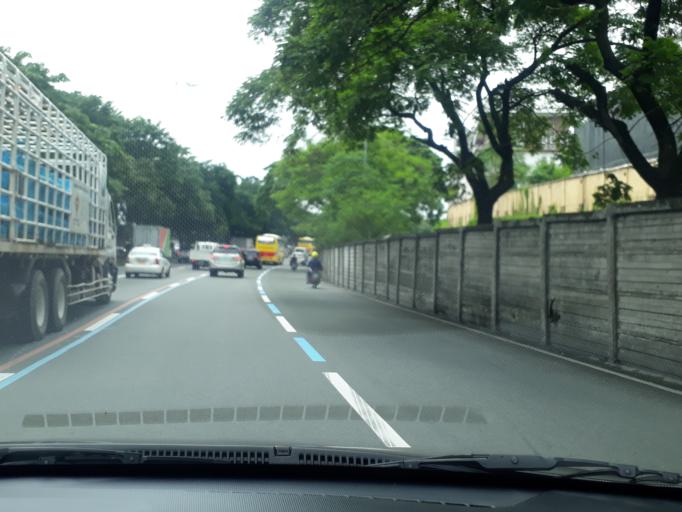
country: PH
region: Calabarzon
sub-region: Province of Rizal
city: Pateros
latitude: 14.5404
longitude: 121.0558
